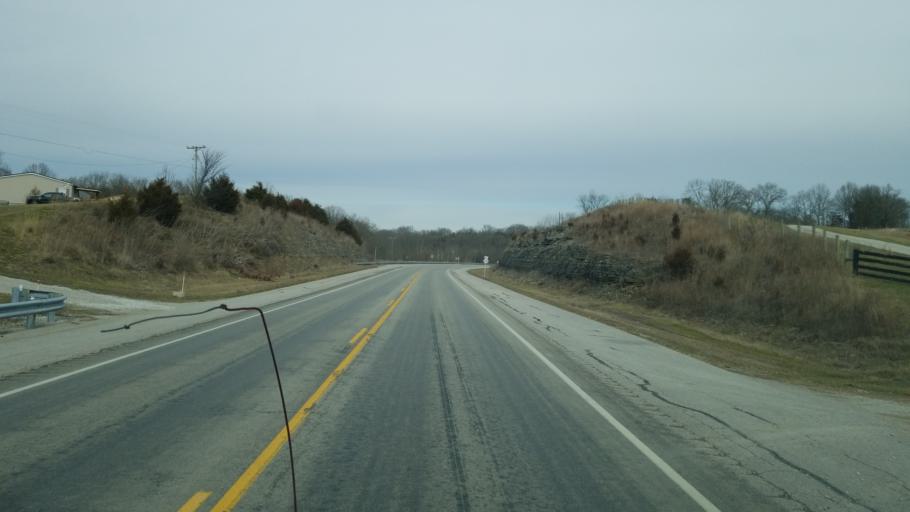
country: US
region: Kentucky
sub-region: Nicholas County
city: Carlisle
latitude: 38.4059
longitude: -84.0134
